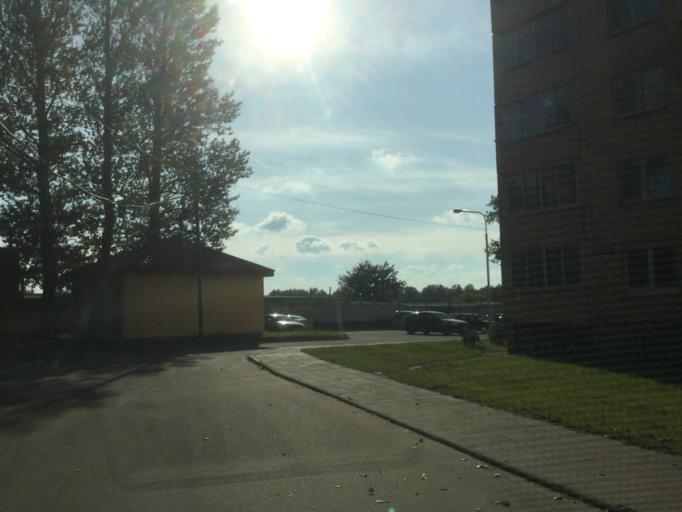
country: BY
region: Vitebsk
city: Vitebsk
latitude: 55.1718
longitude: 30.1940
